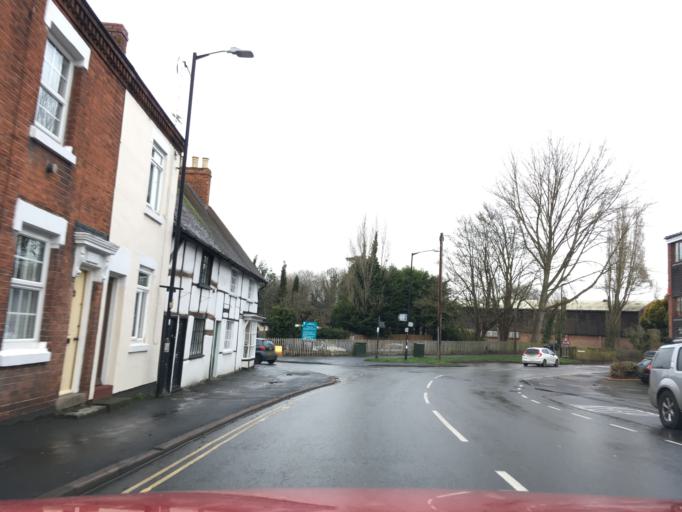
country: GB
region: England
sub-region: Warwickshire
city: Alcester
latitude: 52.2168
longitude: -1.8683
